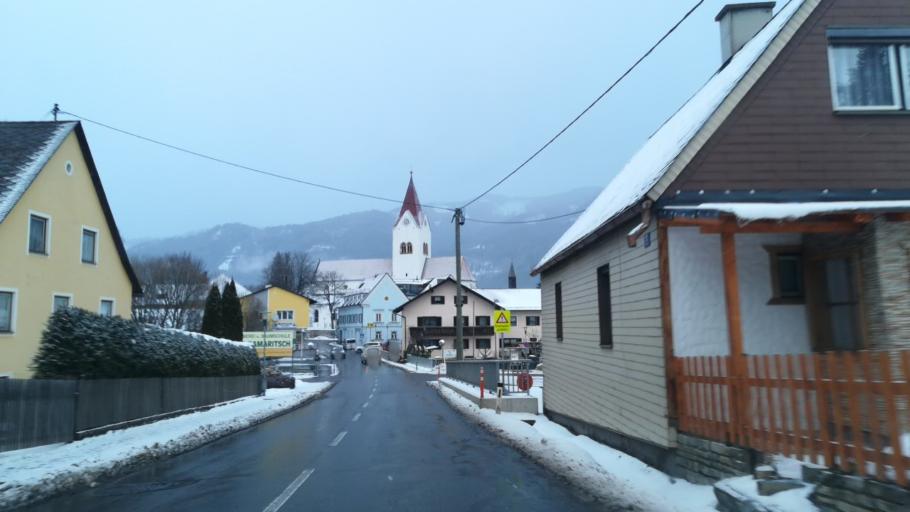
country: AT
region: Styria
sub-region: Politischer Bezirk Murtal
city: Poels
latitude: 47.2186
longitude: 14.5810
